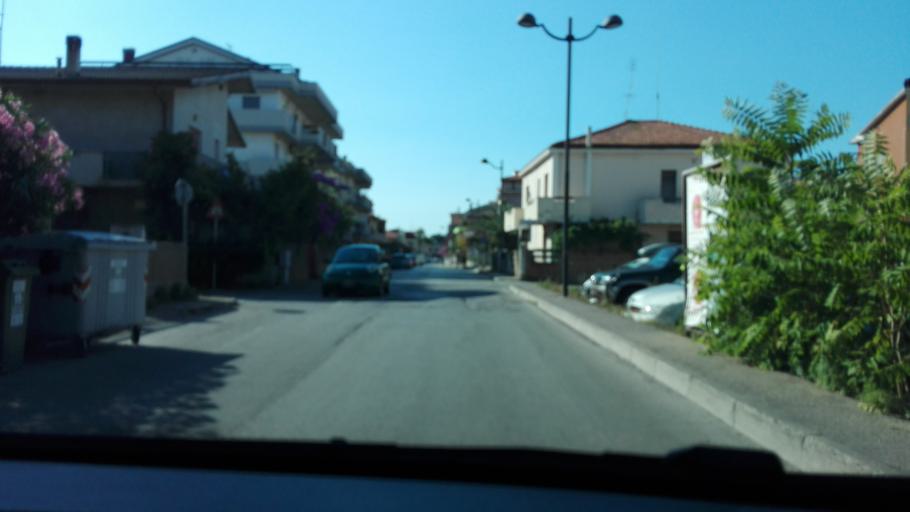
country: IT
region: Abruzzo
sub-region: Provincia di Pescara
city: Montesilvano Marina
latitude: 42.5097
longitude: 14.1642
